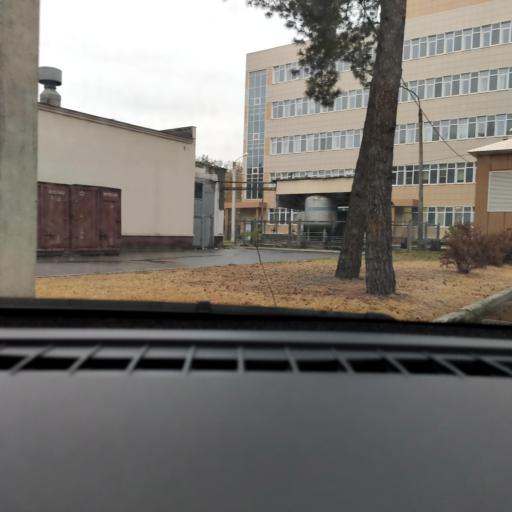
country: RU
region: Voronezj
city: Podgornoye
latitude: 51.7408
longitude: 39.1760
